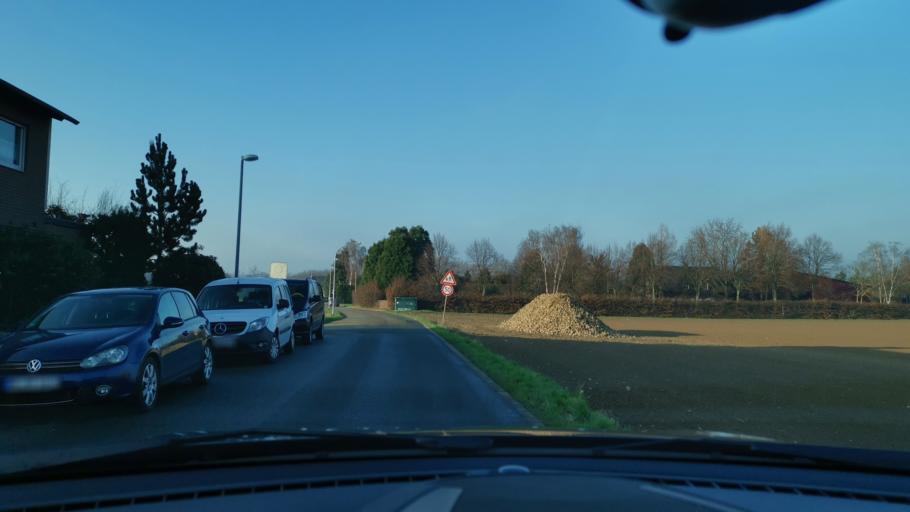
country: DE
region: North Rhine-Westphalia
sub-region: Regierungsbezirk Dusseldorf
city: Neubrueck
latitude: 51.1255
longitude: 6.6768
